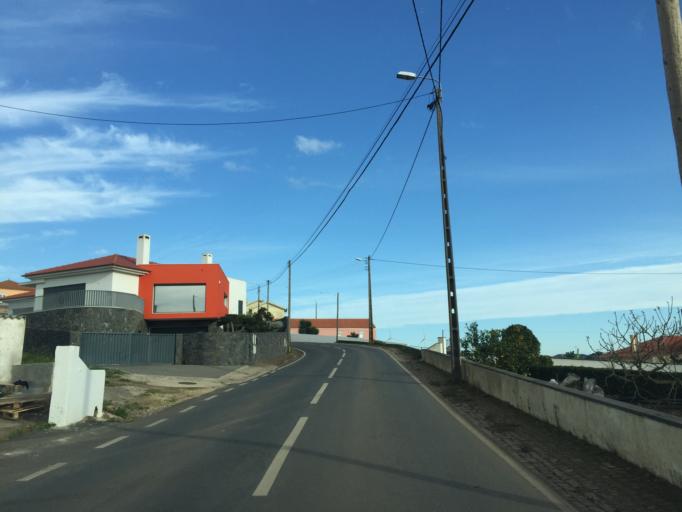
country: PT
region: Lisbon
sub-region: Sintra
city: Almargem
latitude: 38.8357
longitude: -9.2536
